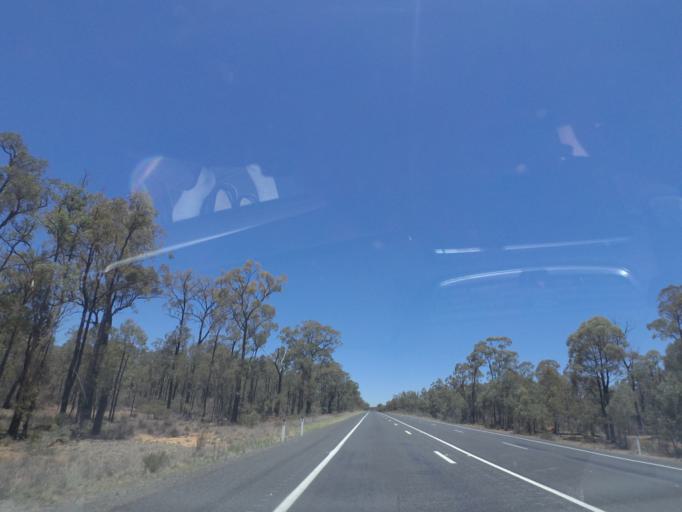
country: AU
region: New South Wales
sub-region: Warrumbungle Shire
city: Coonabarabran
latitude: -30.8745
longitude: 149.4488
